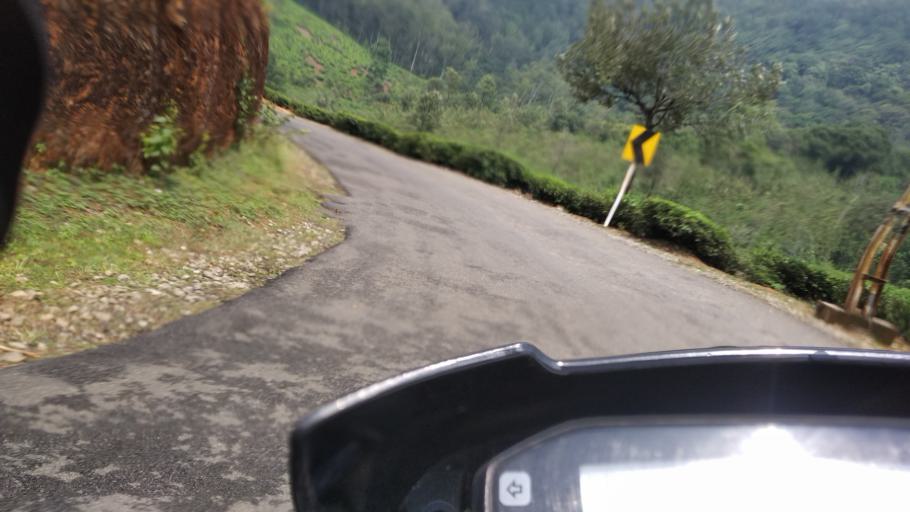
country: IN
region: Kerala
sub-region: Kottayam
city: Erattupetta
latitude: 9.6246
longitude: 76.9724
